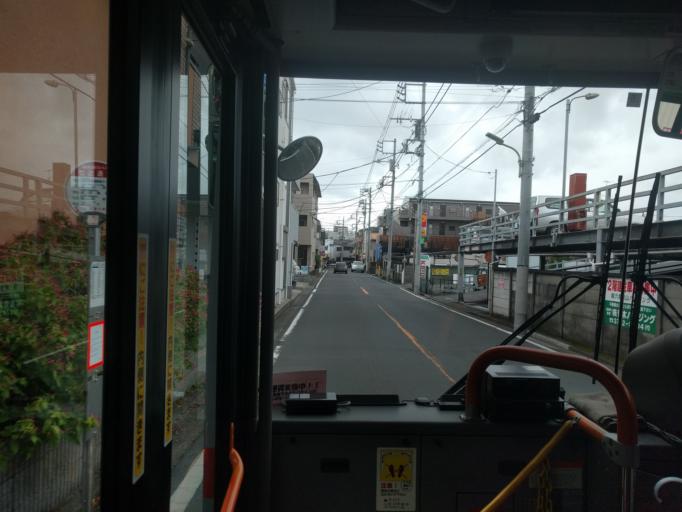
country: JP
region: Kanagawa
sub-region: Kawasaki-shi
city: Kawasaki
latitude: 35.5512
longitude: 139.7222
